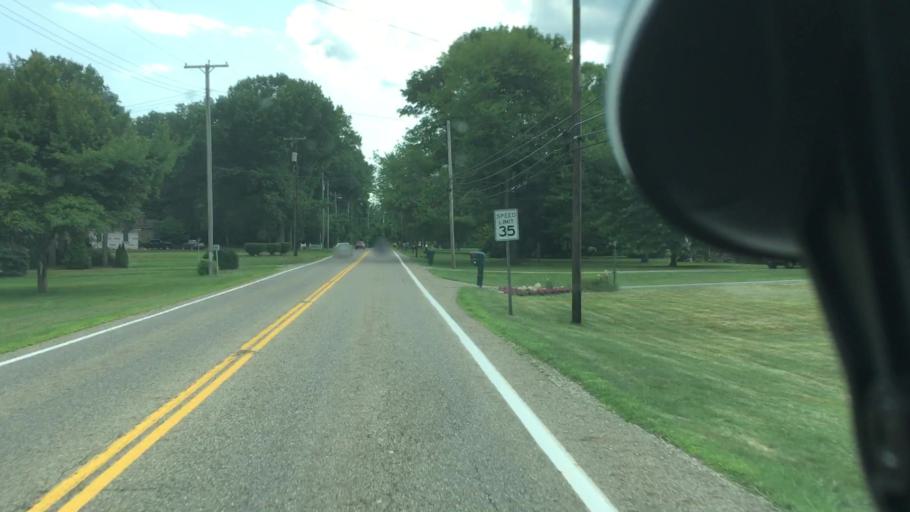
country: US
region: Ohio
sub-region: Columbiana County
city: Salem
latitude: 40.9173
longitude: -80.8412
